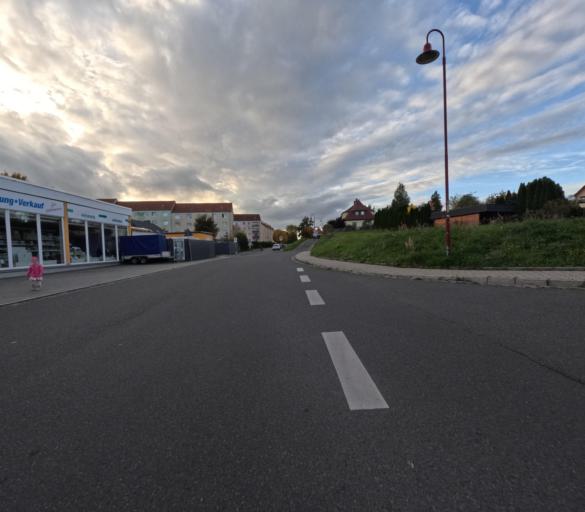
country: DE
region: Saxony
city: Grimma
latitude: 51.2374
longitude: 12.7125
